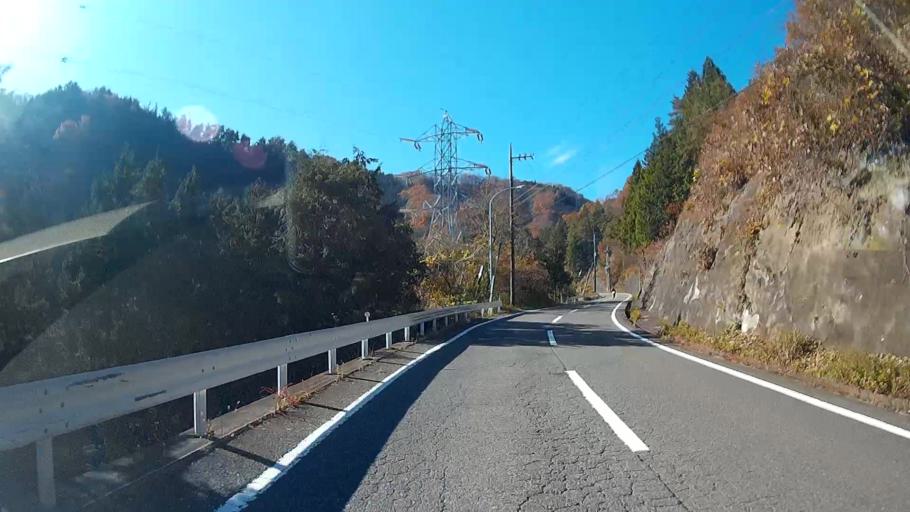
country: JP
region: Yamanashi
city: Otsuki
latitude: 35.5698
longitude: 139.0168
